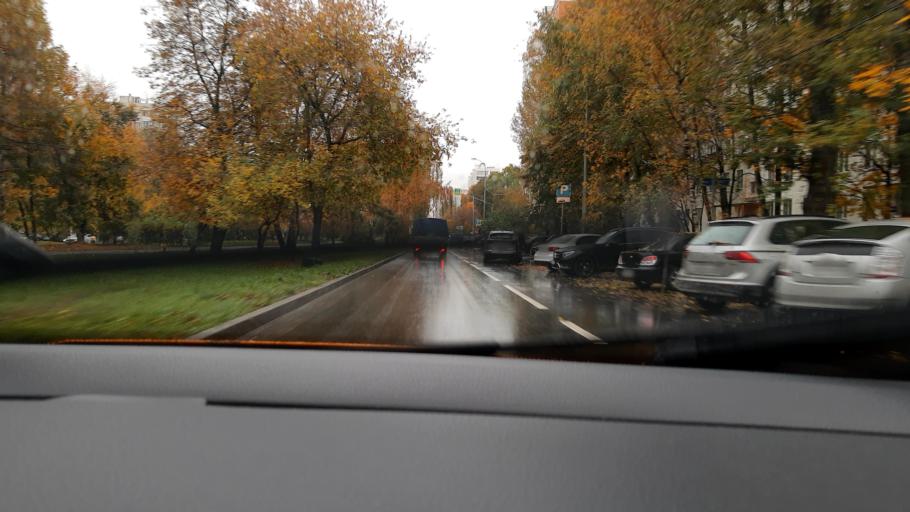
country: RU
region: Moscow
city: Kozeyevo
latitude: 55.8778
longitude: 37.6406
